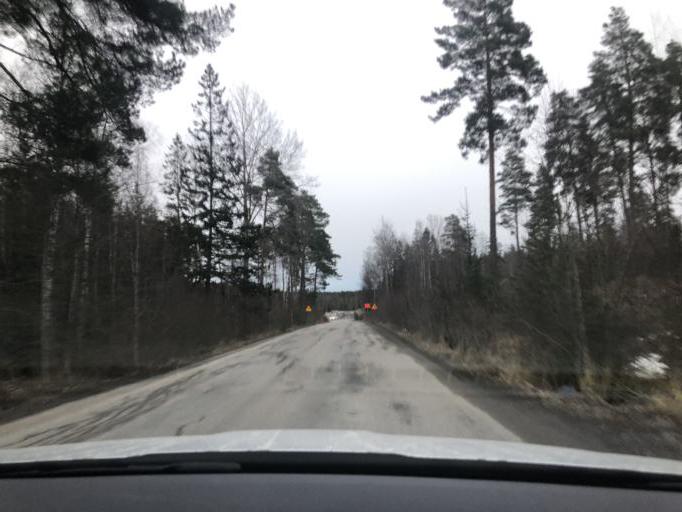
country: SE
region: Stockholm
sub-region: Botkyrka Kommun
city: Tullinge
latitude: 59.1899
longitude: 17.9253
